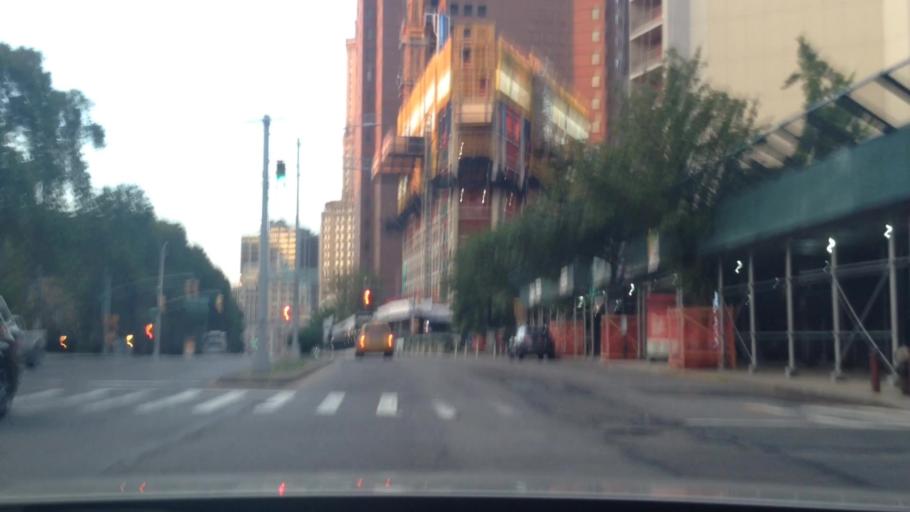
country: US
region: New York
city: New York City
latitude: 40.6971
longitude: -73.9914
